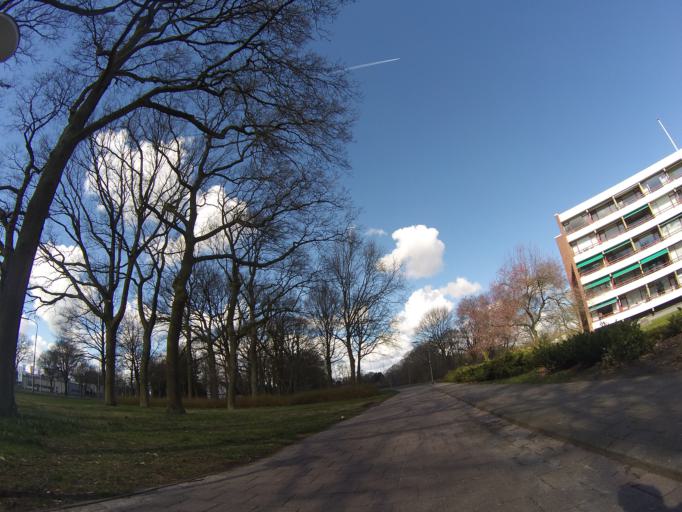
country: NL
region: Drenthe
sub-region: Gemeente Emmen
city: Emmen
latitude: 52.7791
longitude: 6.9153
